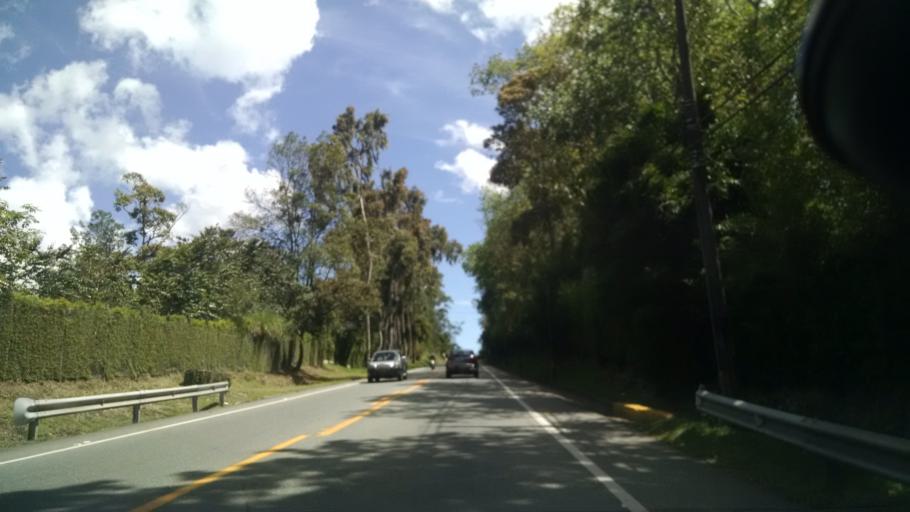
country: CO
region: Antioquia
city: El Retiro
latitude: 6.0974
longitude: -75.5040
